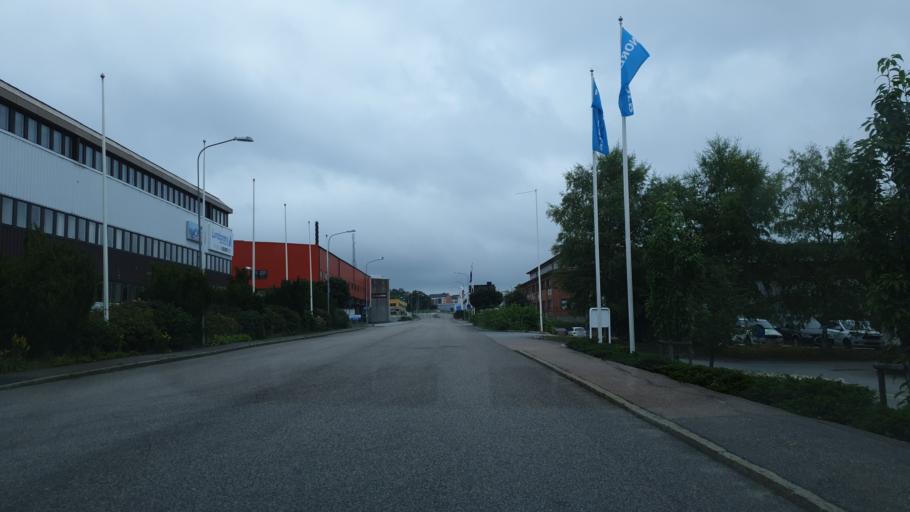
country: SE
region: Vaestra Goetaland
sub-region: Molndal
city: Moelndal
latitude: 57.6390
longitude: 11.9580
